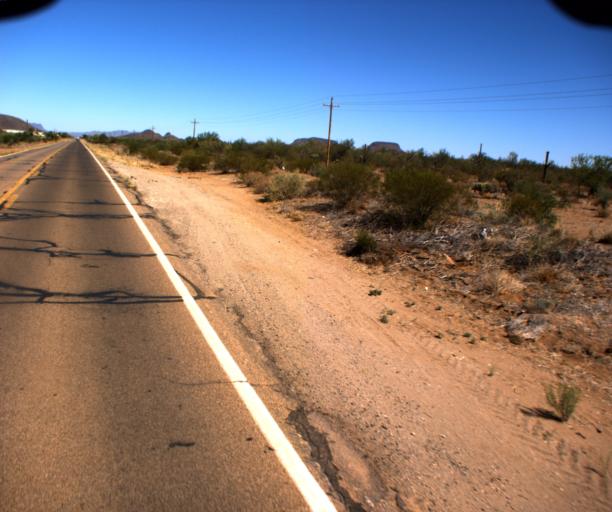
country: US
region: Arizona
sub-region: Pima County
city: Sells
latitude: 31.9304
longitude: -111.9069
